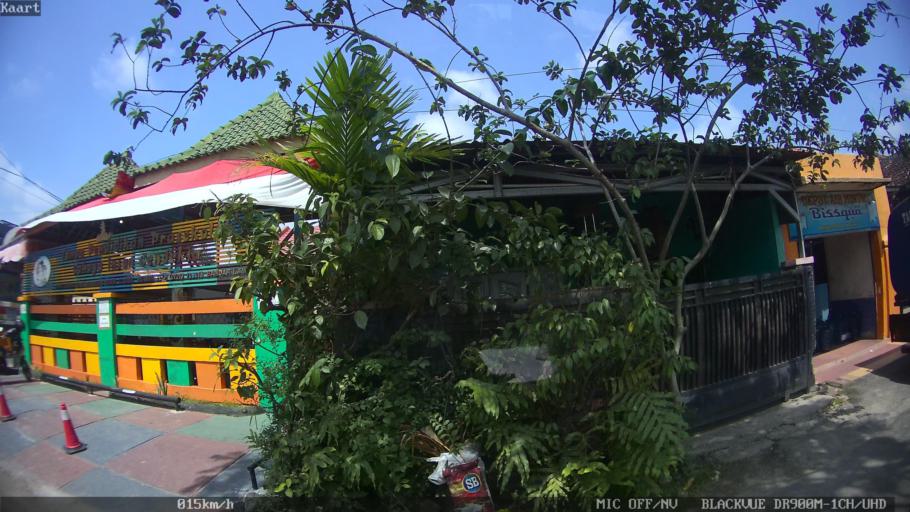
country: ID
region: Lampung
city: Kedaton
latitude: -5.3607
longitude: 105.2811
